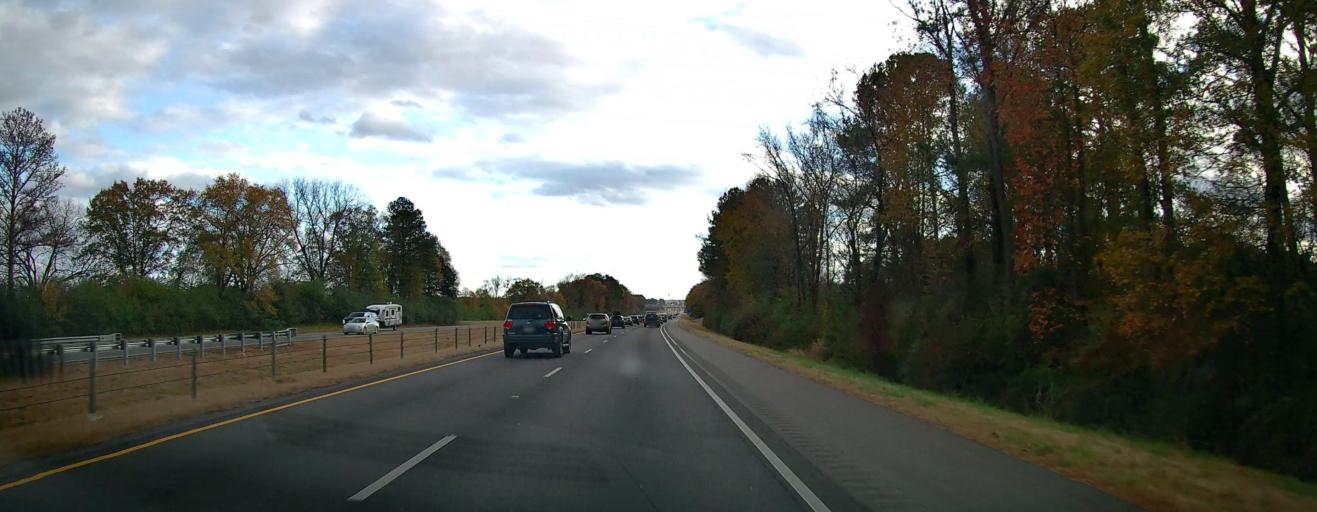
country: US
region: Alabama
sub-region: Cullman County
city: Good Hope
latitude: 34.1484
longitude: -86.8699
